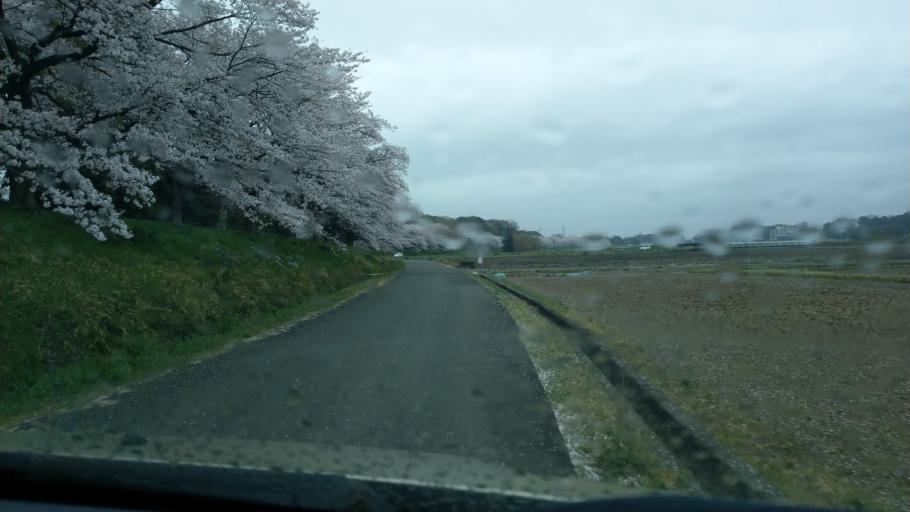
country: JP
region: Saitama
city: Saitama
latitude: 35.9149
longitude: 139.6900
